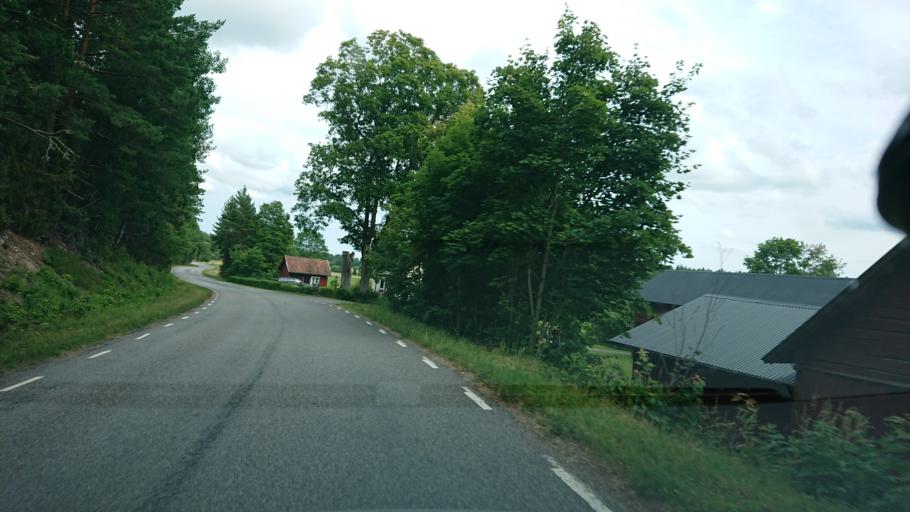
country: SE
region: Uppsala
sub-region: Osthammars Kommun
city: Bjorklinge
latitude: 60.0037
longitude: 17.4552
